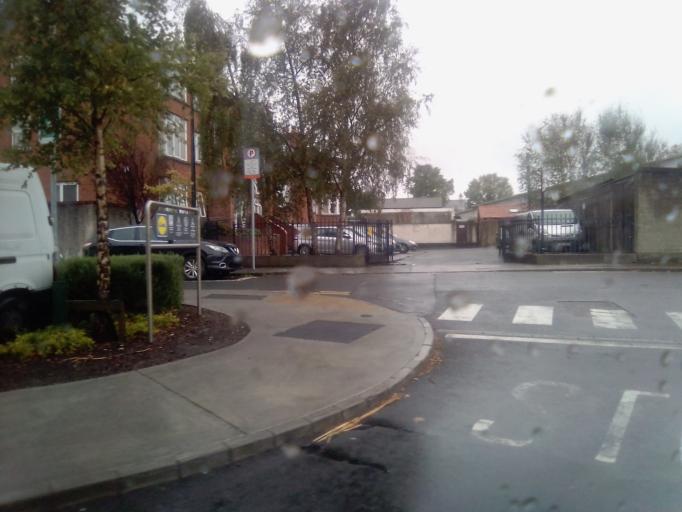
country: IE
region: Leinster
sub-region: South Dublin
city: Terenure
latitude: 53.3090
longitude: -6.2831
